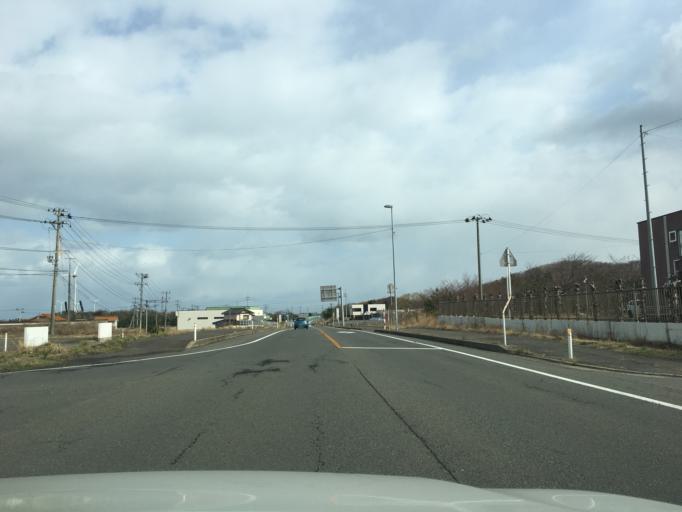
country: JP
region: Yamagata
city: Yuza
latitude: 39.2691
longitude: 139.9231
